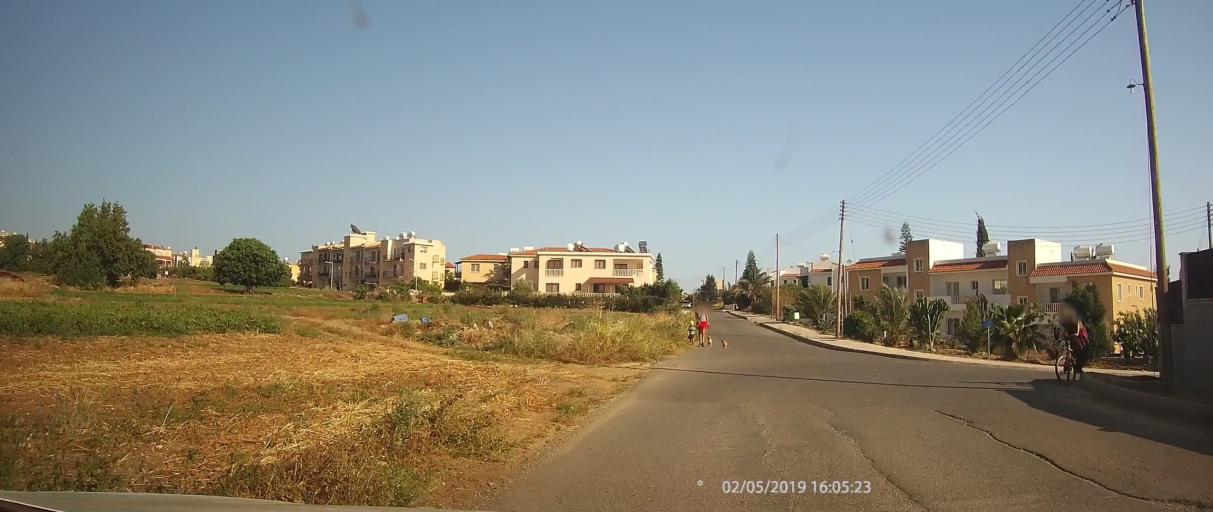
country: CY
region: Pafos
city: Empa
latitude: 34.8167
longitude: 32.4200
